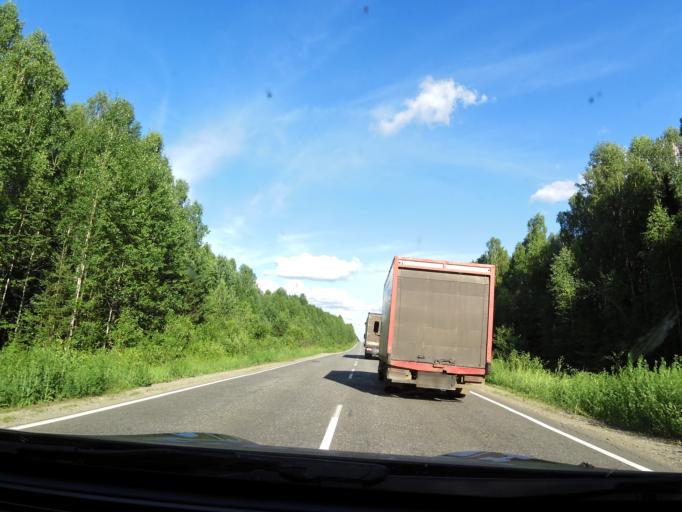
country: RU
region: Kirov
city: Omutninsk
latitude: 58.7659
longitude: 51.9817
